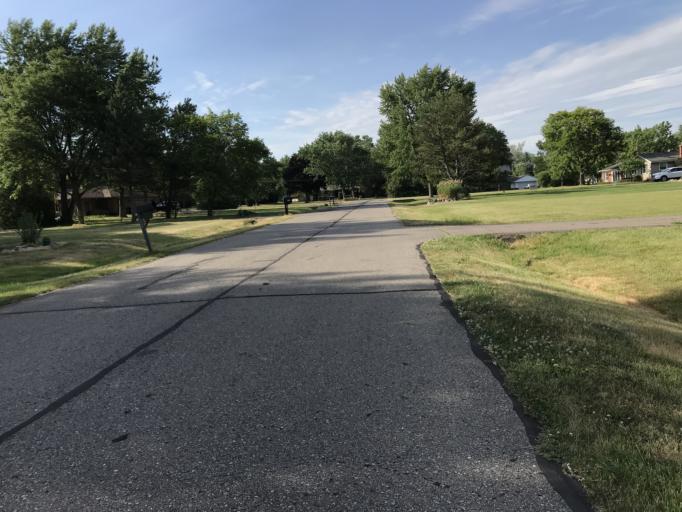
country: US
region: Michigan
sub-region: Oakland County
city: Farmington
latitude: 42.4744
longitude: -83.3293
